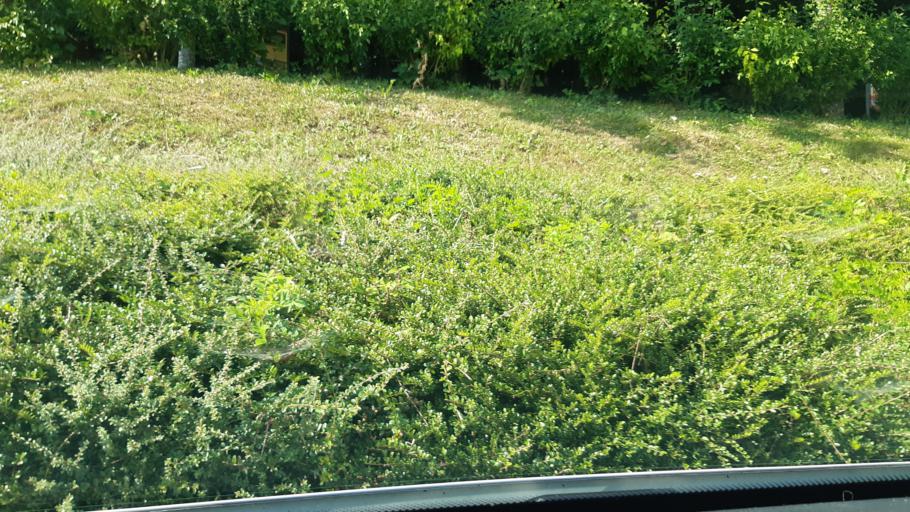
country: SI
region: Lukovica
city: Lukovica pri Domzalah
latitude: 46.1710
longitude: 14.6859
